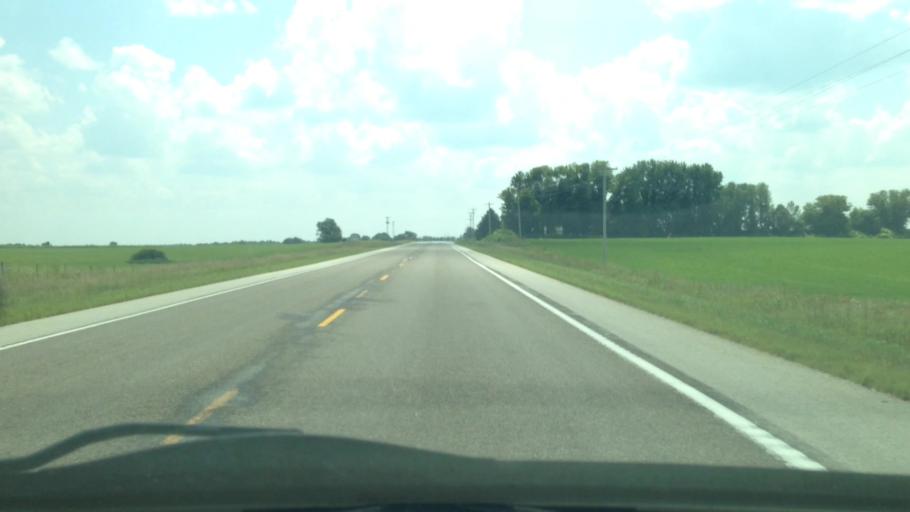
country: US
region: Minnesota
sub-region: Olmsted County
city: Stewartville
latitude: 43.9094
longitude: -92.4086
